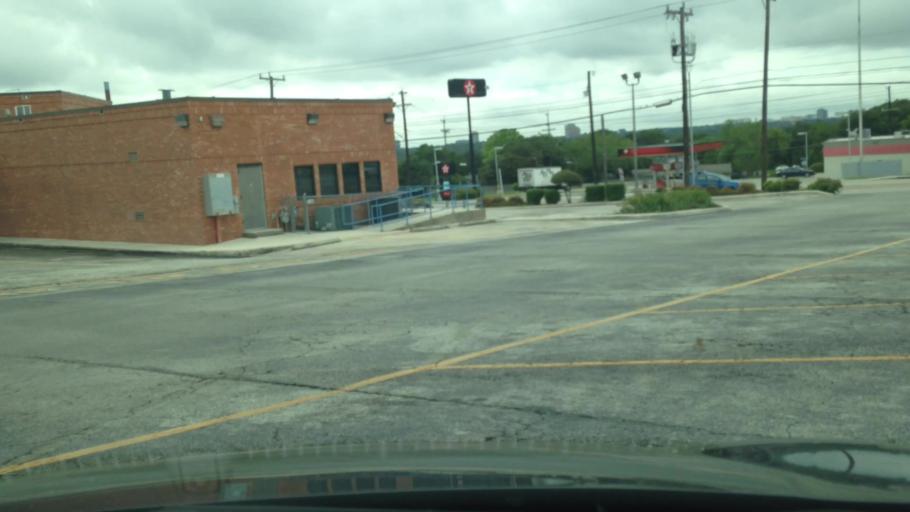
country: US
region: Texas
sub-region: Bexar County
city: Castle Hills
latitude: 29.5428
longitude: -98.5277
